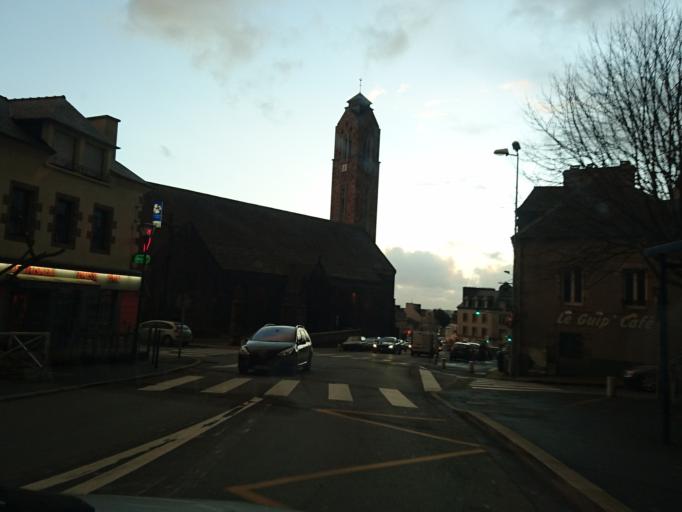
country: FR
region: Brittany
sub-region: Departement du Finistere
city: Guipavas
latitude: 48.4350
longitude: -4.4007
